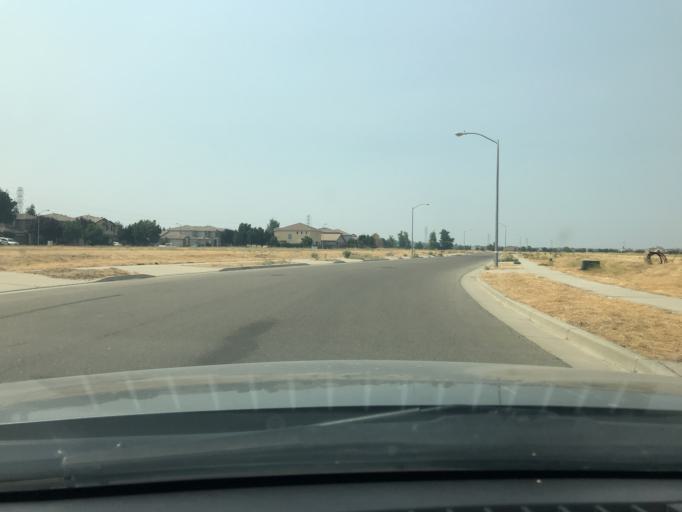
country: US
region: California
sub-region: Merced County
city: Merced
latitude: 37.3449
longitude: -120.4820
